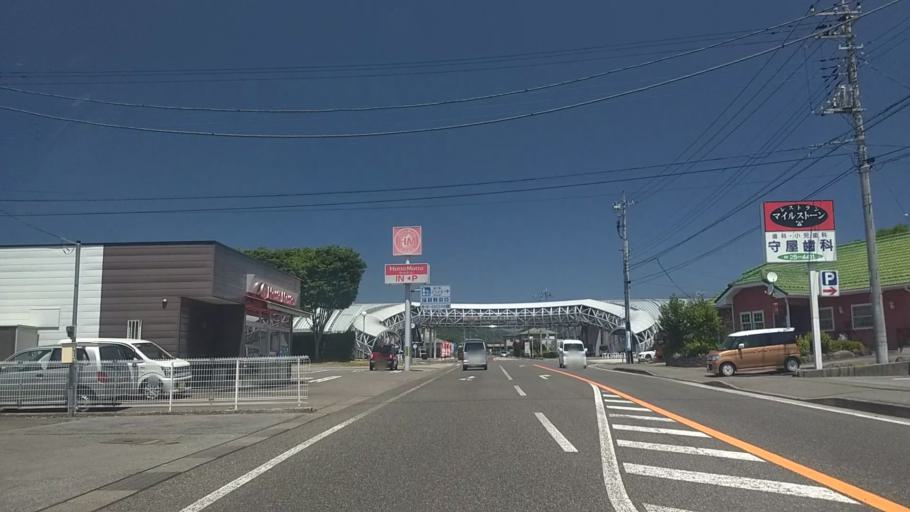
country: JP
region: Yamanashi
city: Nirasaki
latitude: 35.7472
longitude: 138.4390
